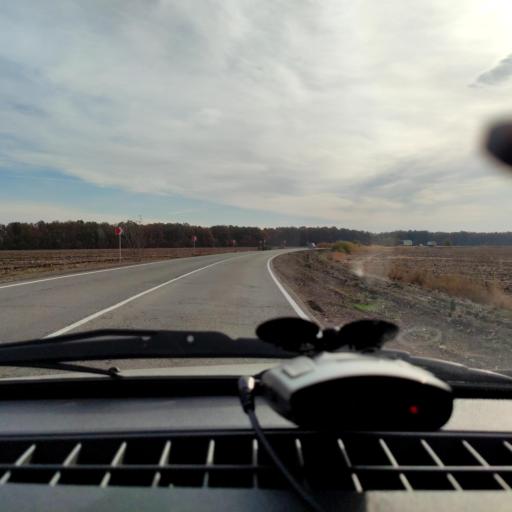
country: RU
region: Voronezj
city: Shilovo
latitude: 51.4517
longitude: 38.9867
